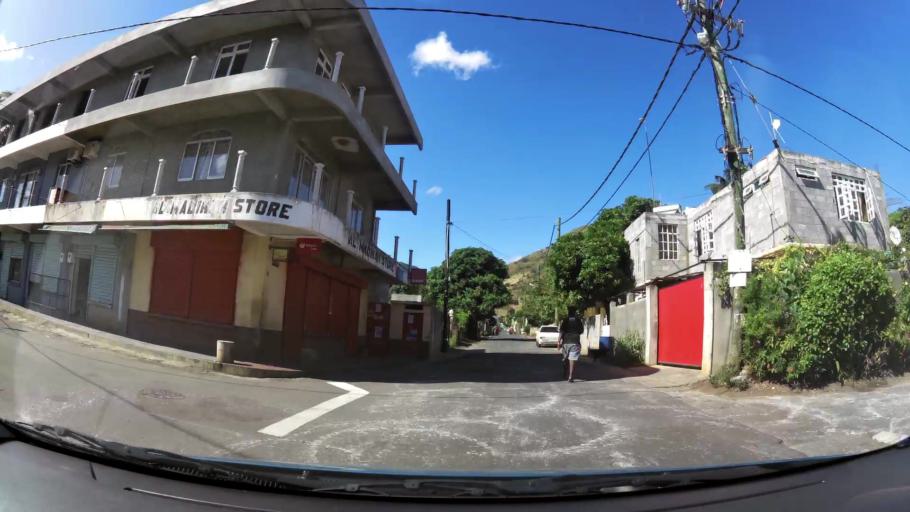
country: MU
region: Black River
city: Cascavelle
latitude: -20.2617
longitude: 57.4178
